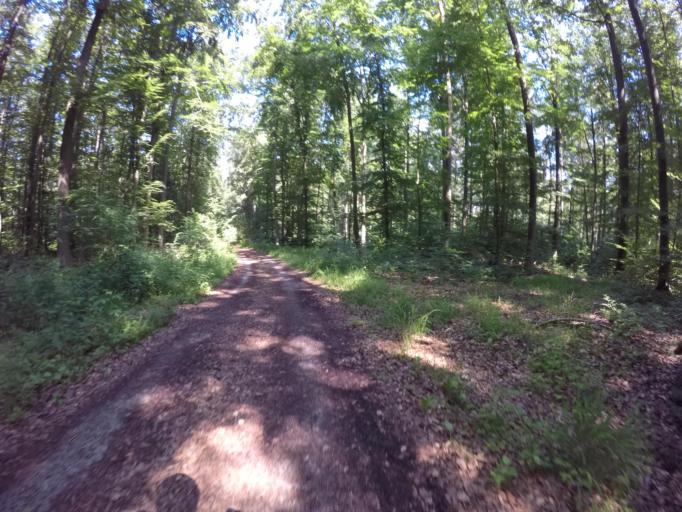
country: DE
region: Bavaria
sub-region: Lower Bavaria
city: Essing
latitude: 48.9135
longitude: 11.8175
